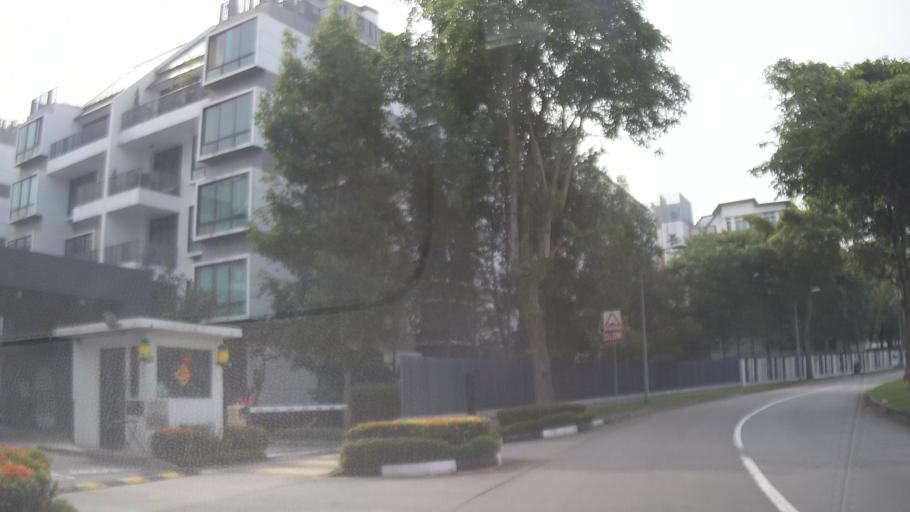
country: MY
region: Johor
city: Johor Bahru
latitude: 1.4294
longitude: 103.7854
